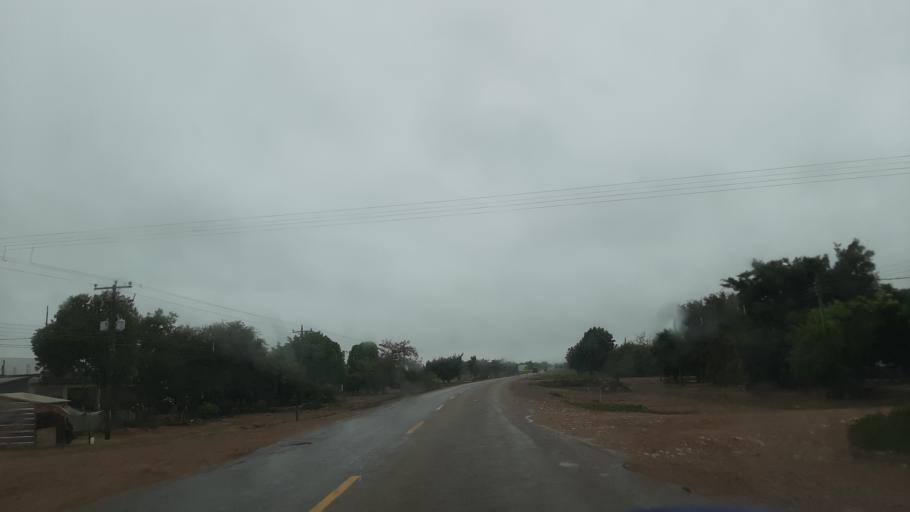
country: BO
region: Santa Cruz
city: Okinawa Numero Uno
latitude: -16.8061
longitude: -62.5996
